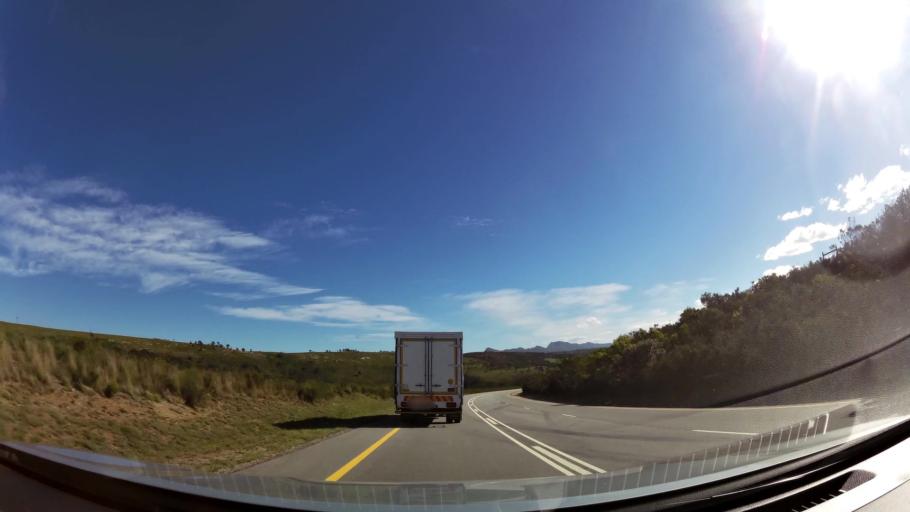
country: ZA
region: Eastern Cape
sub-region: Cacadu District Municipality
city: Kruisfontein
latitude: -34.0416
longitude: 24.5841
